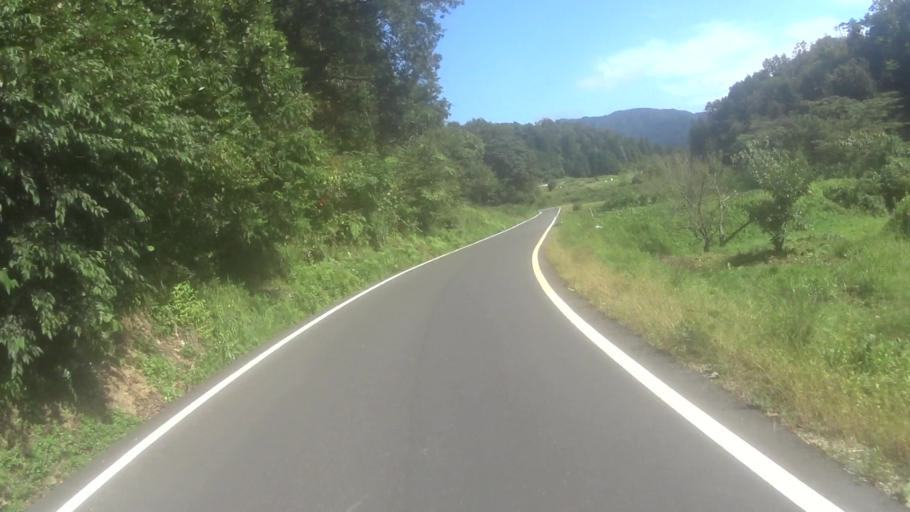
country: JP
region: Kyoto
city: Miyazu
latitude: 35.6119
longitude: 135.1183
